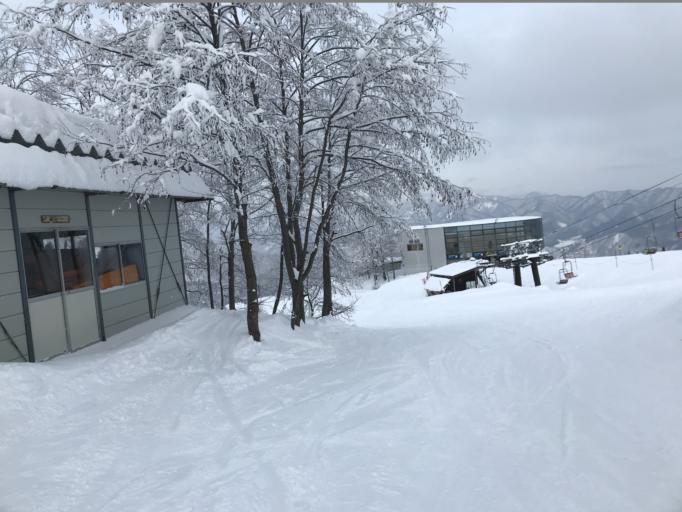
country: JP
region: Nagano
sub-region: Kitaazumi Gun
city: Hakuba
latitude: 36.7025
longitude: 137.8193
